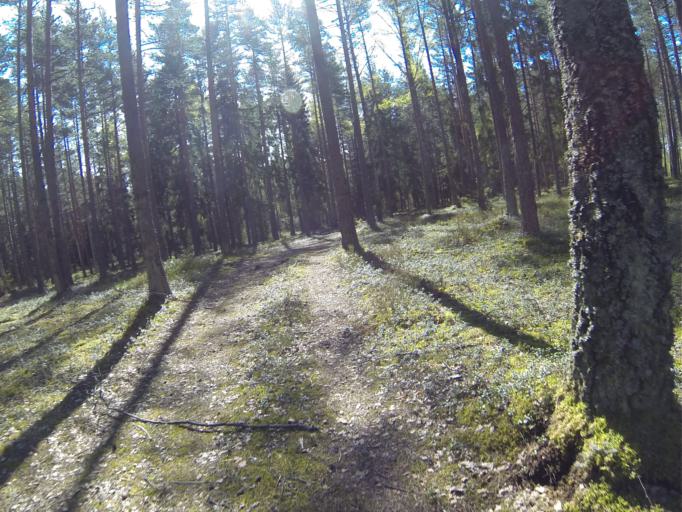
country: FI
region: Varsinais-Suomi
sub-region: Salo
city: Salo
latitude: 60.3968
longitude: 23.1973
